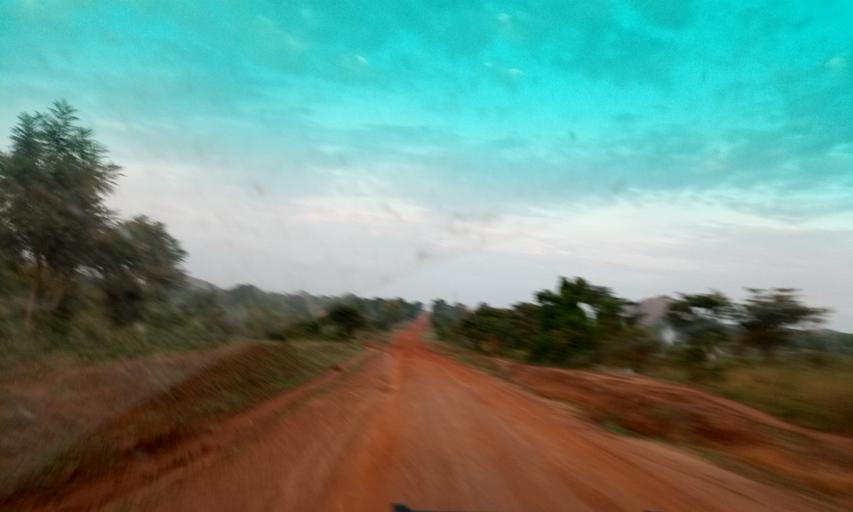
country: UG
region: Eastern Region
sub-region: Ngora District
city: Ngora
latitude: 1.4672
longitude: 33.8122
